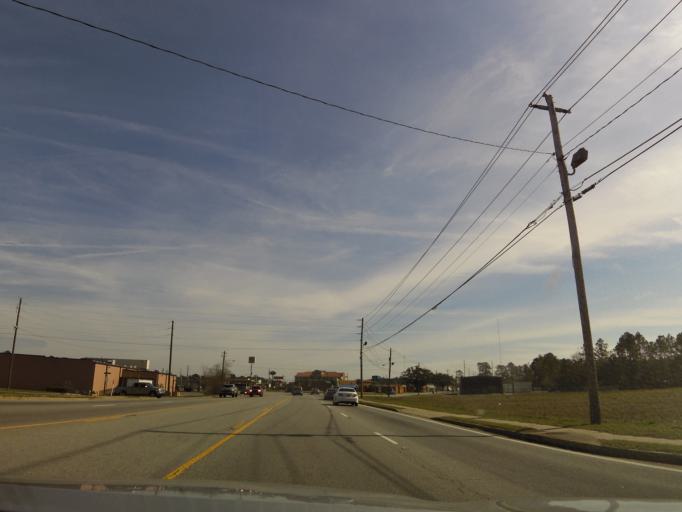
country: US
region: Georgia
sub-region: Ware County
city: Waycross
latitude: 31.2060
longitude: -82.3407
